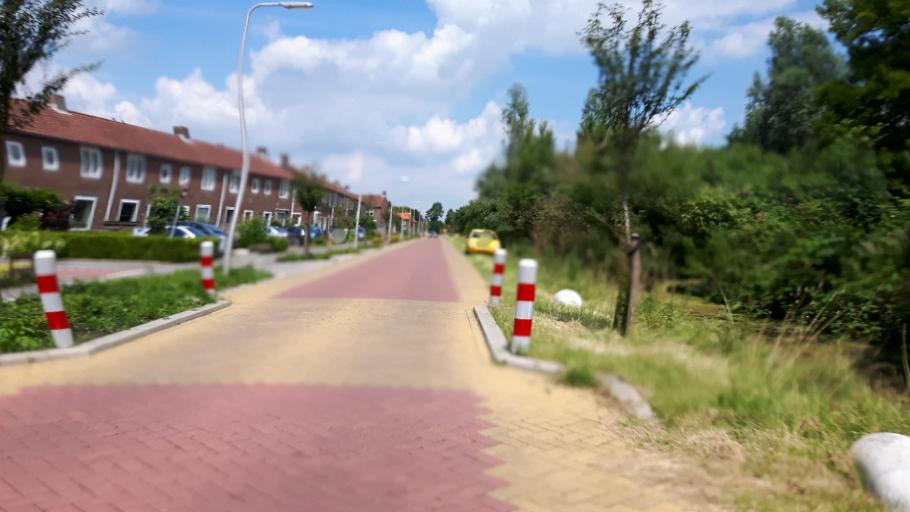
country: NL
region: South Holland
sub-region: Gemeente Boskoop
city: Boskoop
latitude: 52.0820
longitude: 4.6805
